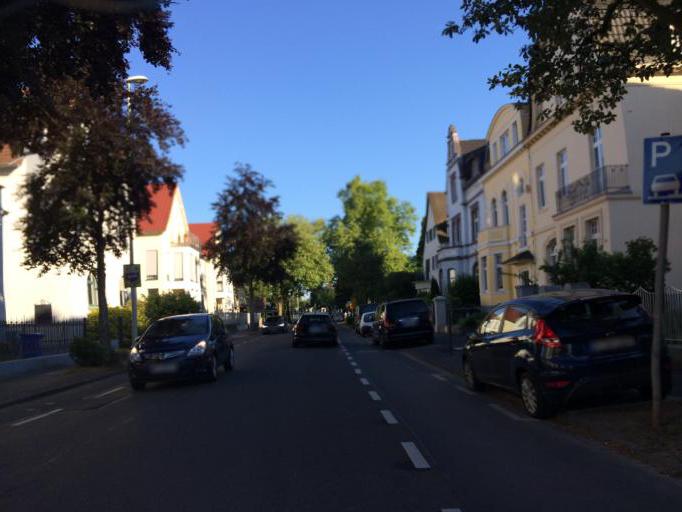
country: DE
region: North Rhine-Westphalia
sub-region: Regierungsbezirk Koln
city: Konigswinter
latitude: 50.6819
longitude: 7.1709
